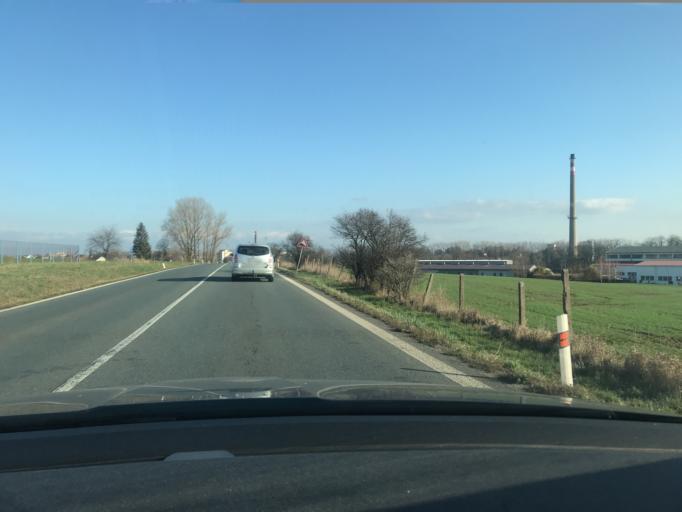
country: CZ
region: Kralovehradecky
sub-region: Okres Hradec Kralove
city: Smirice
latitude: 50.3104
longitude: 15.8616
